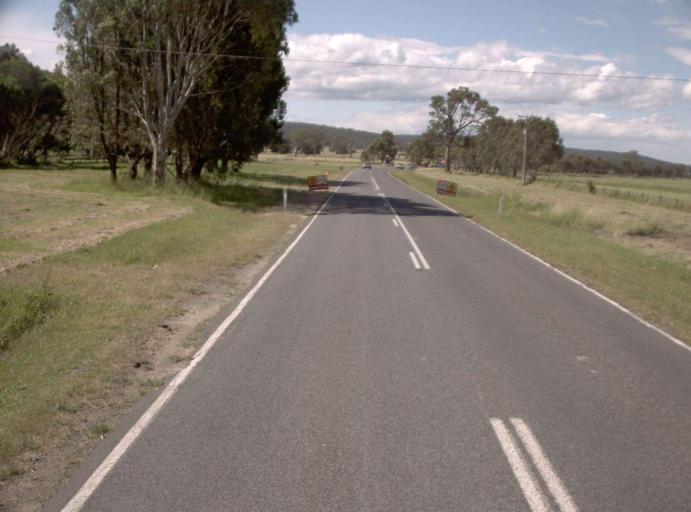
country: AU
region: Victoria
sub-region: Latrobe
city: Traralgon
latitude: -38.1492
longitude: 146.5231
